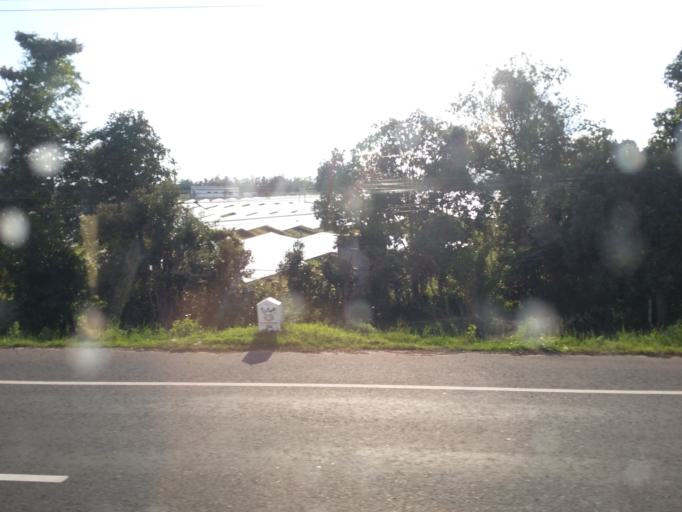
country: TH
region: Changwat Ubon Ratchathani
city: Sirindhorn
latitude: 15.1957
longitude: 105.3689
